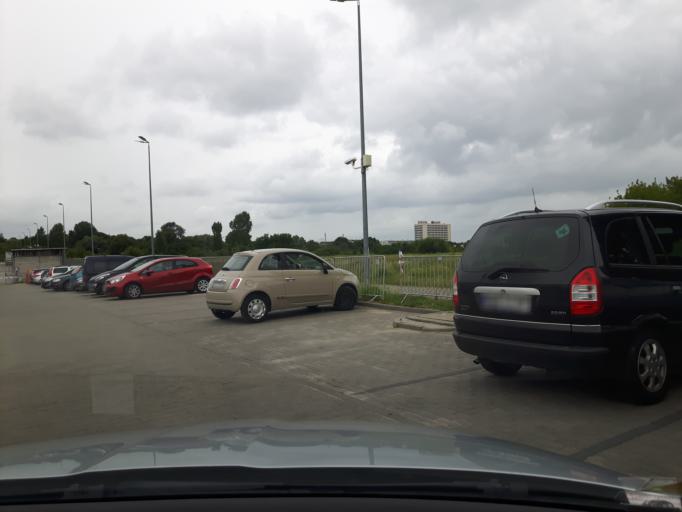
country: PL
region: Pomeranian Voivodeship
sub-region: Sopot
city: Sopot
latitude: 54.4258
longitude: 18.5830
